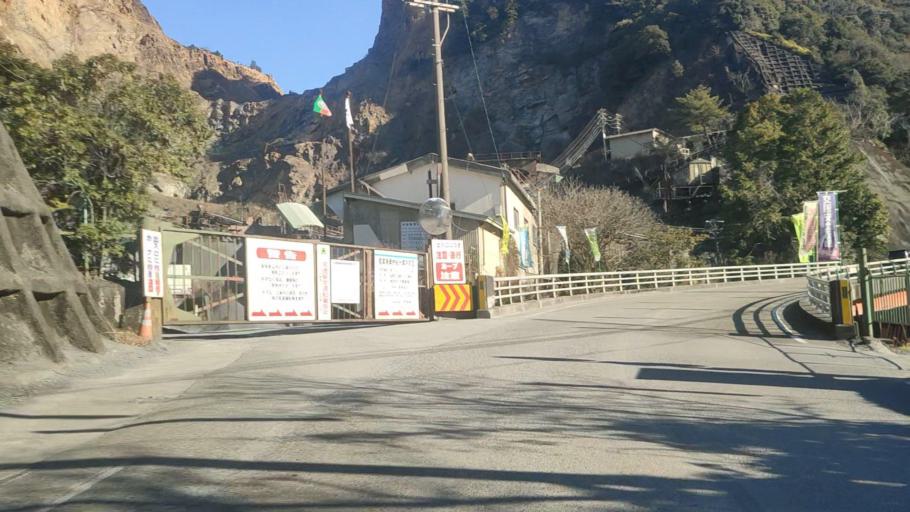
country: JP
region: Miyazaki
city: Nobeoka
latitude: 32.6285
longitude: 131.7174
